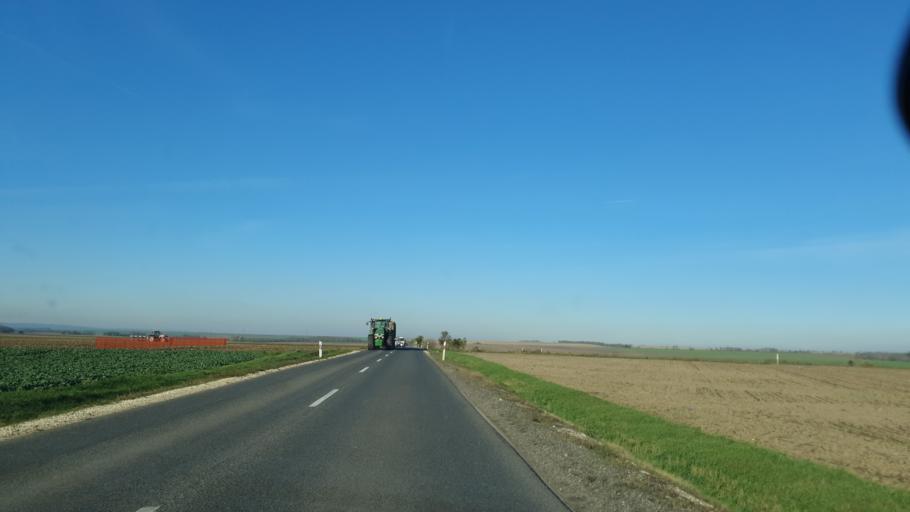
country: HU
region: Fejer
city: Szekesfehervar
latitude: 47.2392
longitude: 18.4175
